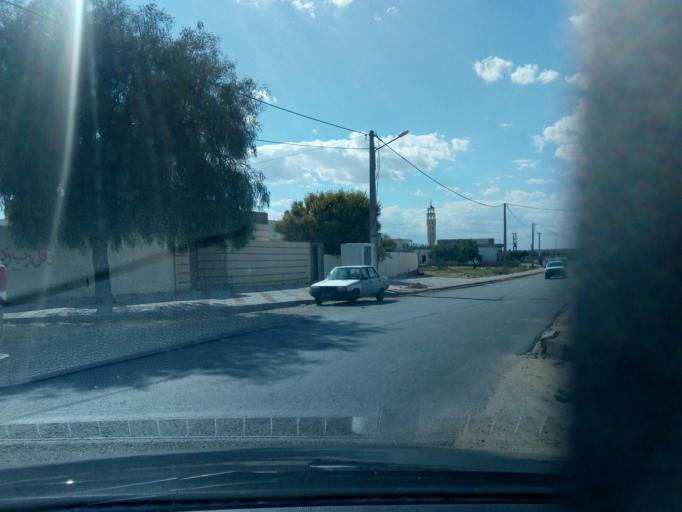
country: TN
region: Safaqis
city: Sfax
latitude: 34.7306
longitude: 10.6050
